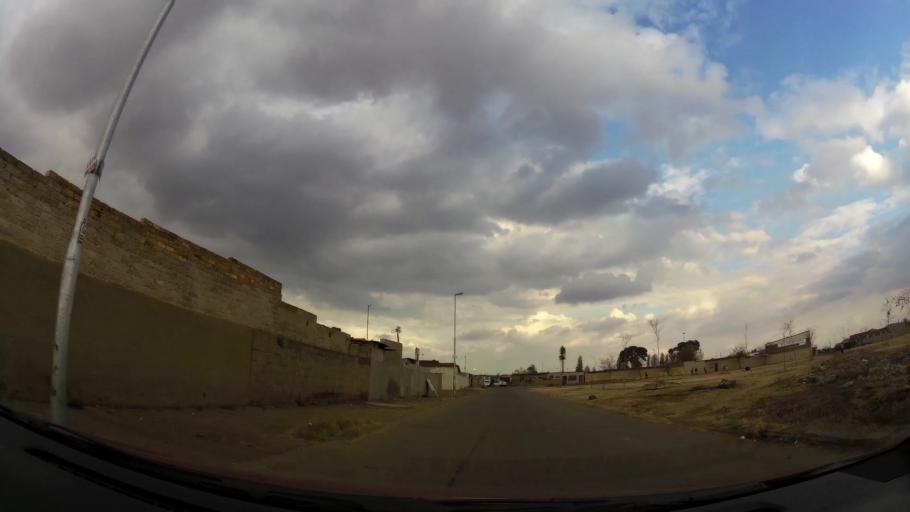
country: ZA
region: Gauteng
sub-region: City of Johannesburg Metropolitan Municipality
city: Soweto
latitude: -26.2427
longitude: 27.8193
